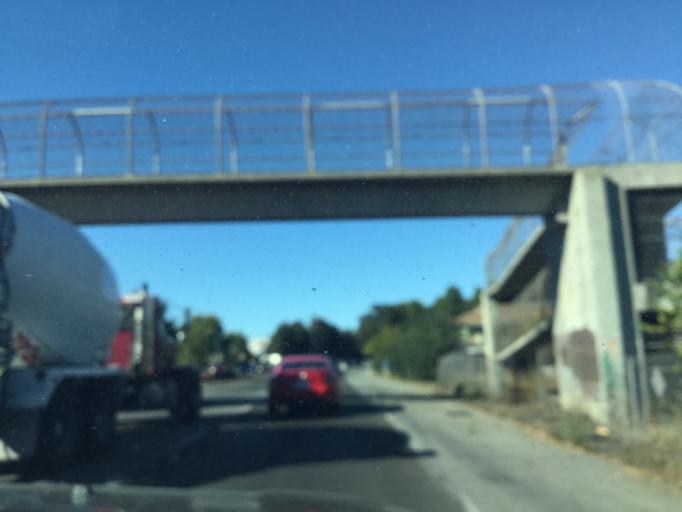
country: US
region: California
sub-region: San Mateo County
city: Redwood City
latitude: 37.4817
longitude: -122.2186
